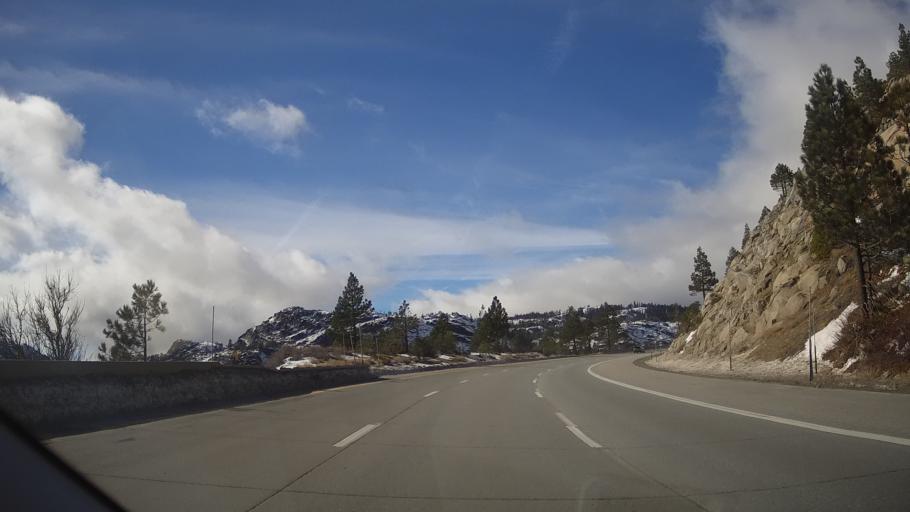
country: US
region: California
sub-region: Nevada County
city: Truckee
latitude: 39.3280
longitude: -120.2976
